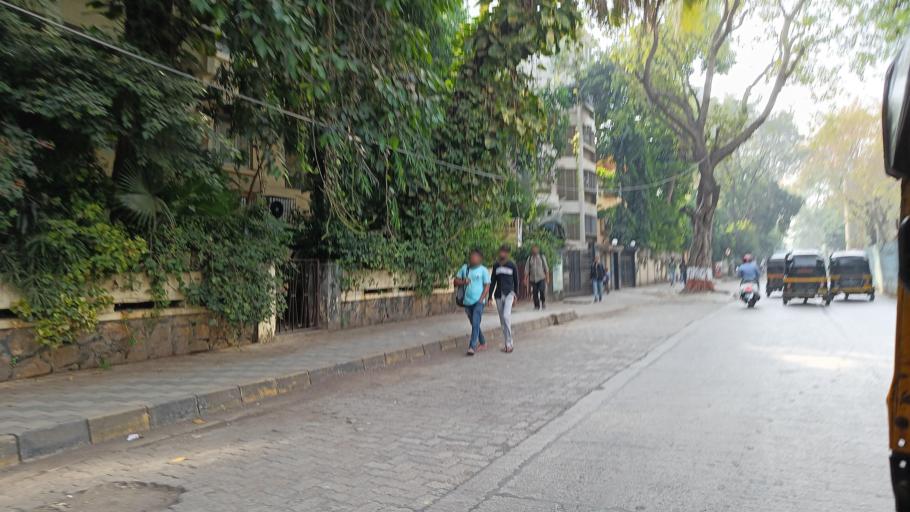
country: IN
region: Maharashtra
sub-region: Mumbai Suburban
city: Mumbai
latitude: 19.1066
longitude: 72.8370
